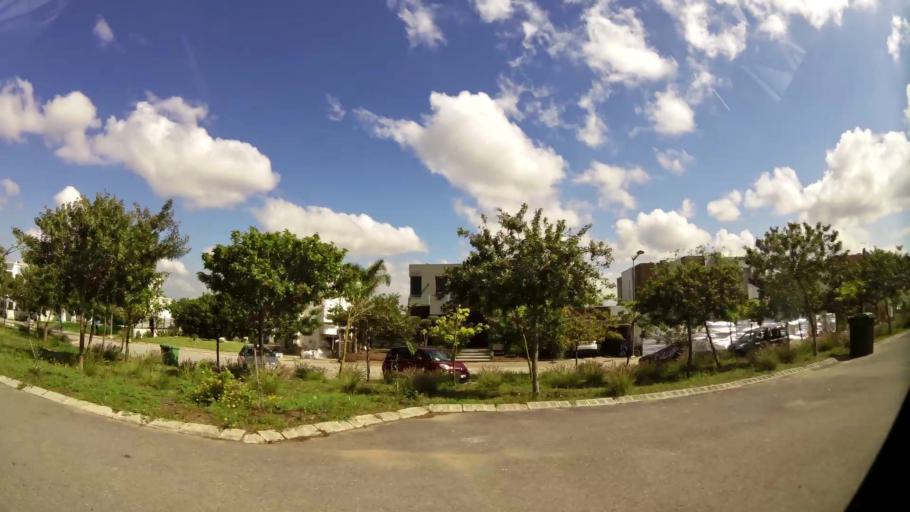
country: MA
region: Grand Casablanca
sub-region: Nouaceur
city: Bouskoura
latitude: 33.4656
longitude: -7.5969
